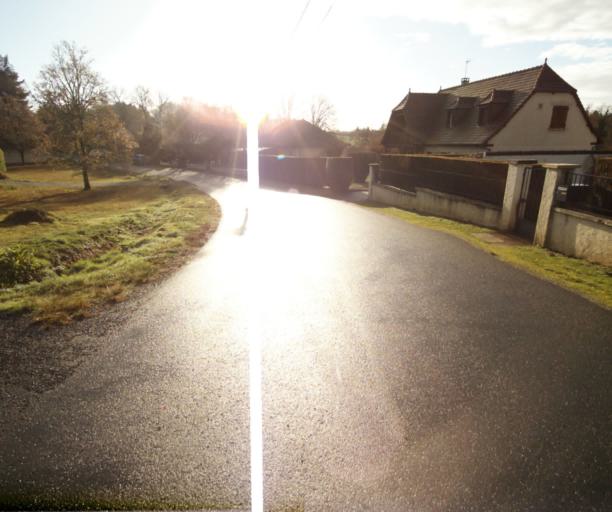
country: FR
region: Limousin
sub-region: Departement de la Correze
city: Saint-Mexant
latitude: 45.2665
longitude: 1.6305
